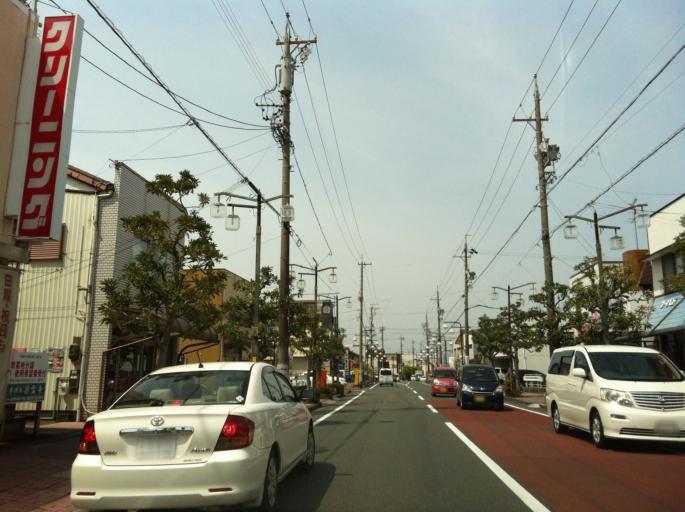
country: JP
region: Shizuoka
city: Kakegawa
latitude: 34.7727
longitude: 138.0096
